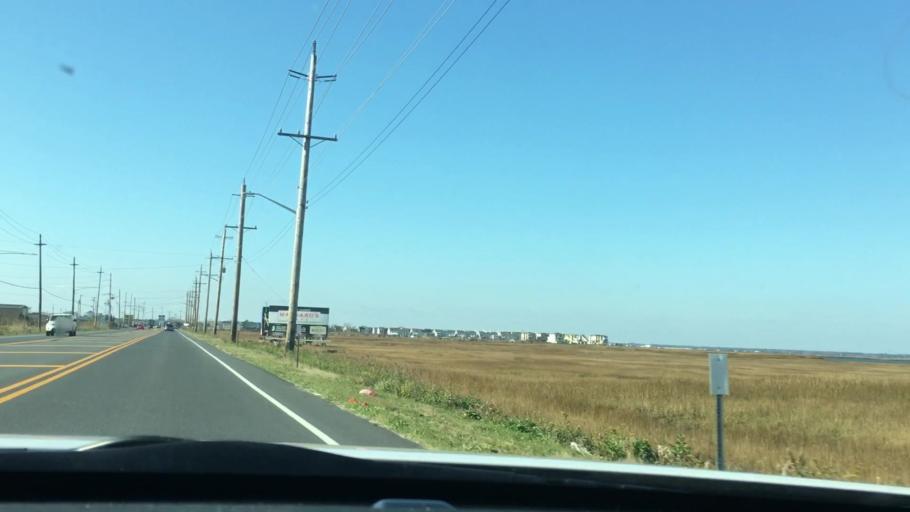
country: US
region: New Jersey
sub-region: Atlantic County
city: Ventnor City
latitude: 39.3562
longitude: -74.4709
